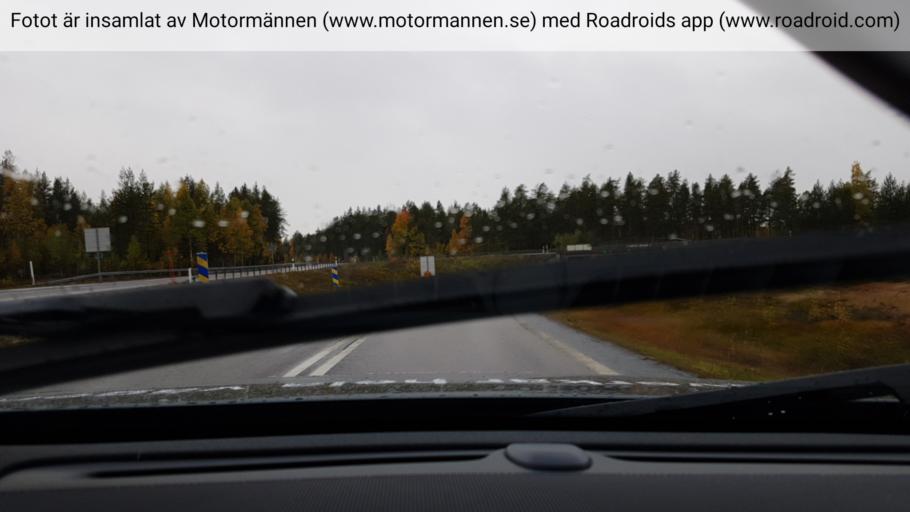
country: SE
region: Norrbotten
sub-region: Lulea Kommun
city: Gammelstad
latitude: 65.5823
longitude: 21.9989
